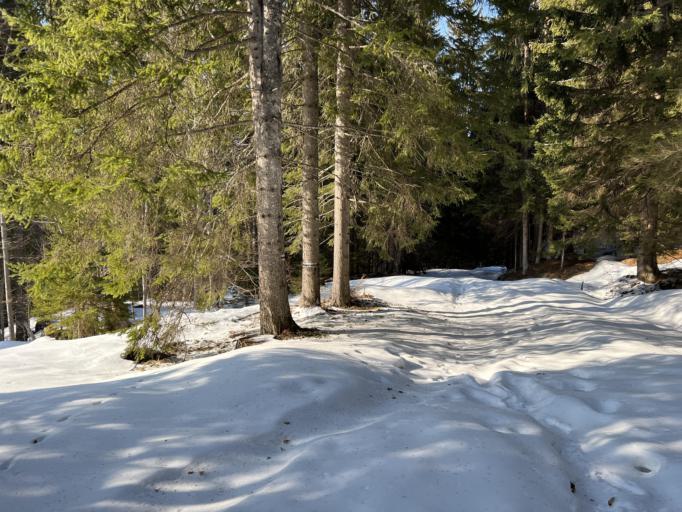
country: AT
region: Carinthia
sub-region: Politischer Bezirk Villach Land
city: Arnoldstein
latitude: 46.5150
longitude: 13.7008
